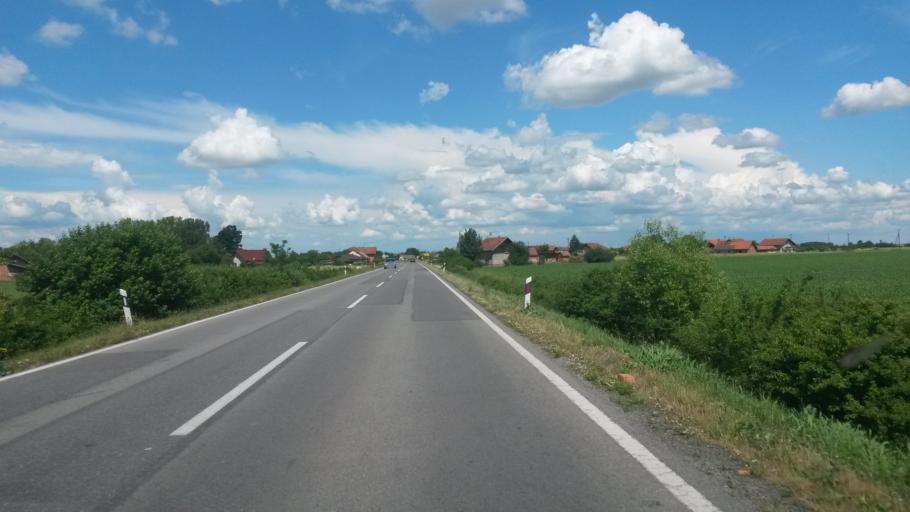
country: HR
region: Osjecko-Baranjska
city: Vuka
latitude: 45.4236
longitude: 18.4949
